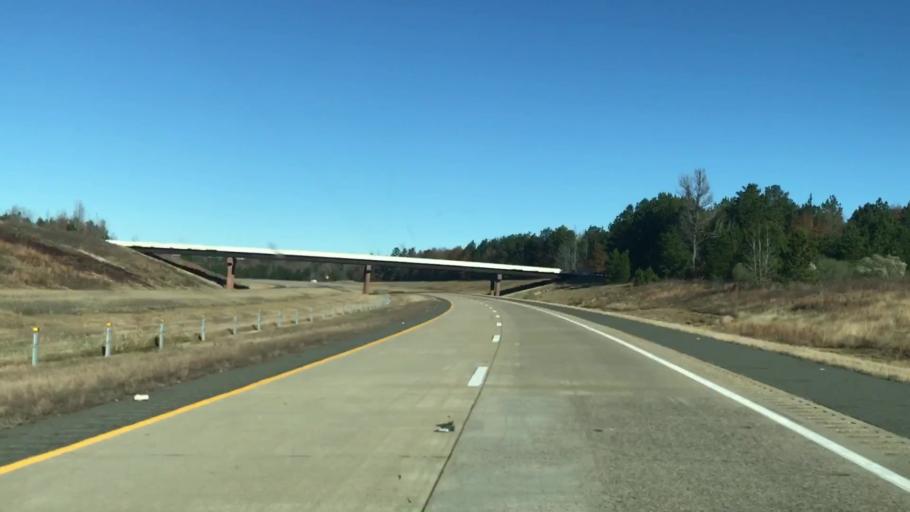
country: US
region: Texas
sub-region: Bowie County
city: Texarkana
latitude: 33.2675
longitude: -93.8976
